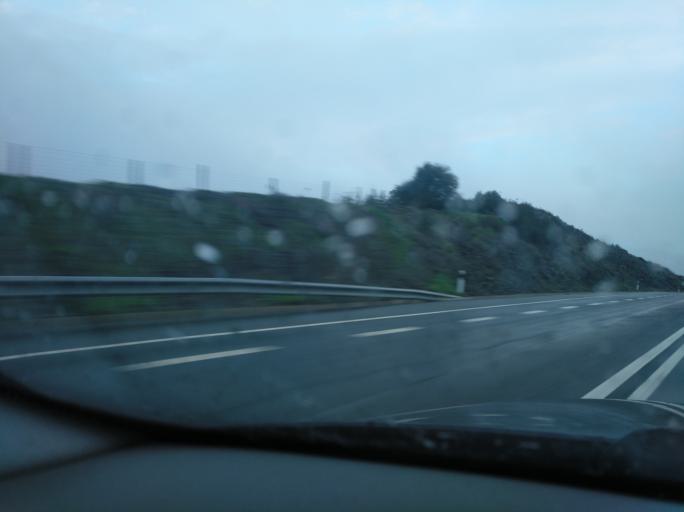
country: PT
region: Faro
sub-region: Castro Marim
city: Castro Marim
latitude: 37.3088
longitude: -7.4907
